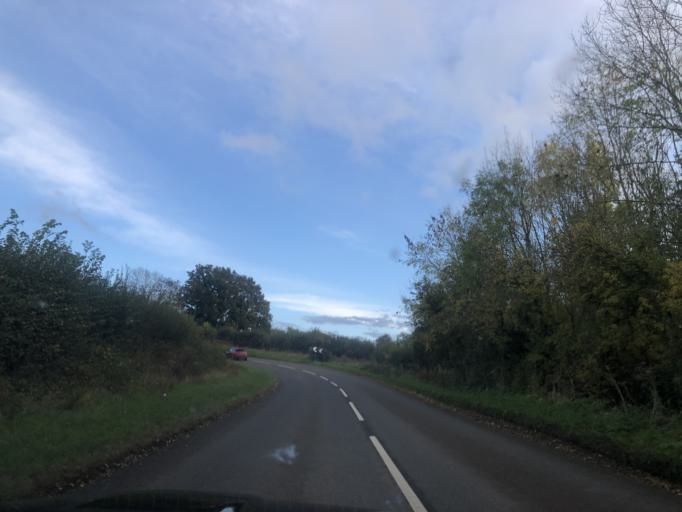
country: GB
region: England
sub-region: Warwickshire
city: Harbury
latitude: 52.2385
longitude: -1.4703
